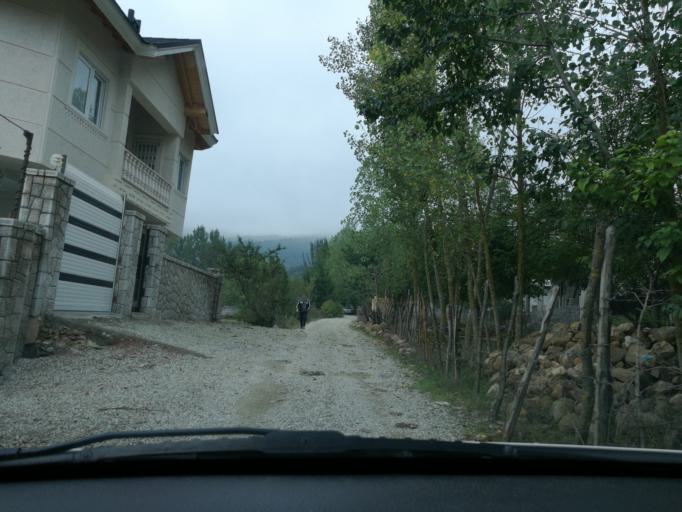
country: IR
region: Mazandaran
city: `Abbasabad
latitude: 36.5003
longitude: 51.2088
